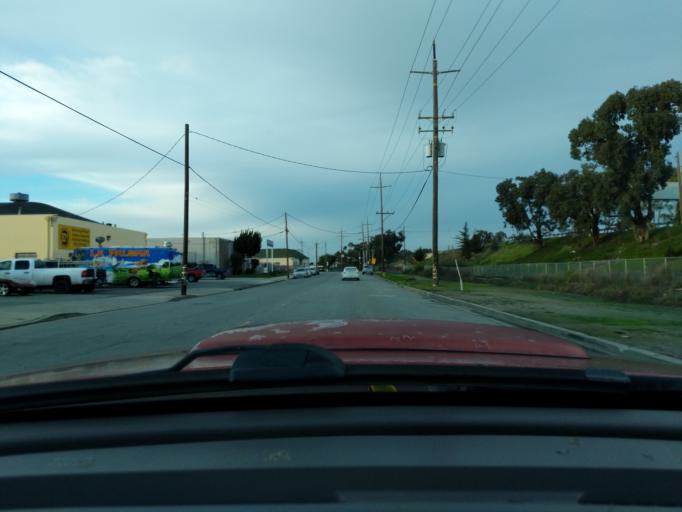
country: US
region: California
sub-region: Monterey County
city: Salinas
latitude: 36.6722
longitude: -121.6411
